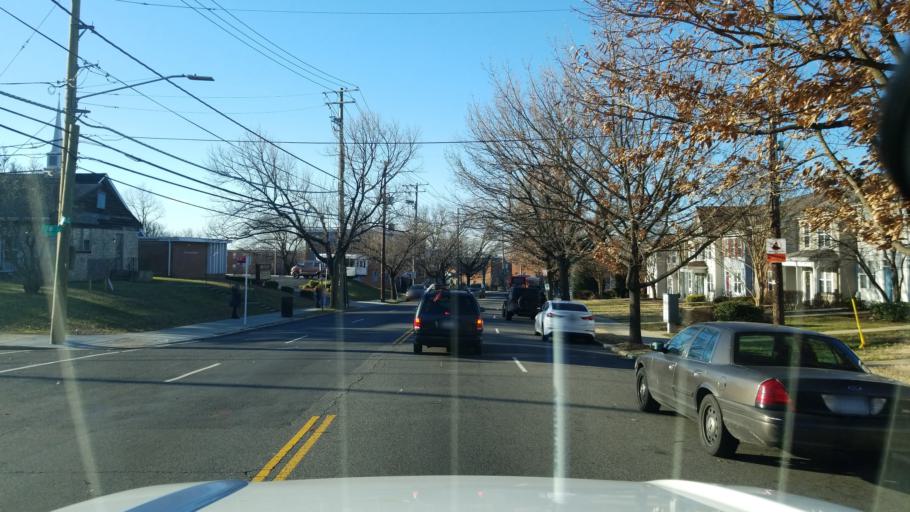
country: US
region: Maryland
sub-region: Prince George's County
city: Hillcrest Heights
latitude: 38.8485
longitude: -76.9781
